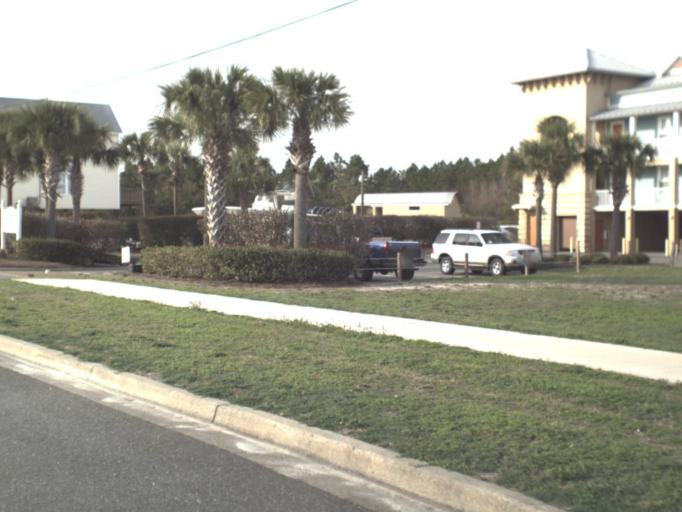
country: US
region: Florida
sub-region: Bay County
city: Mexico Beach
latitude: 29.9525
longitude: -85.4254
